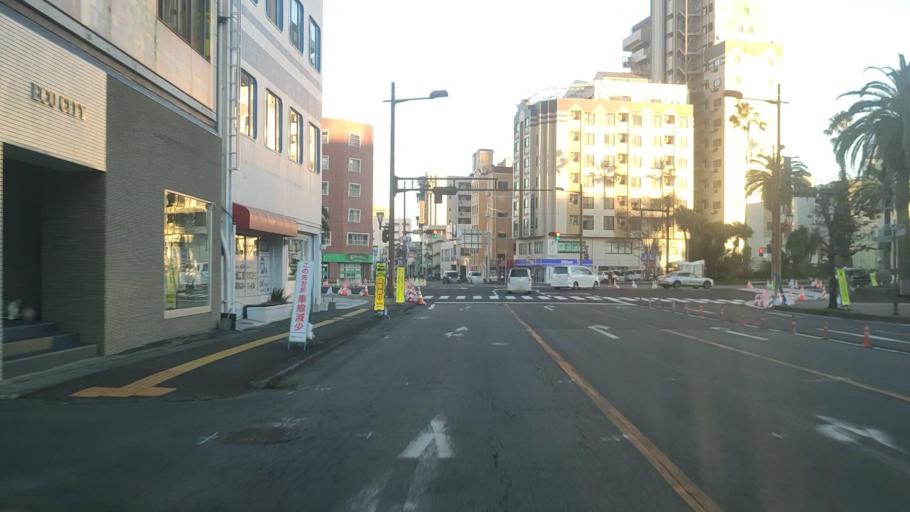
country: JP
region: Miyazaki
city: Miyazaki-shi
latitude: 31.9085
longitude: 131.4212
